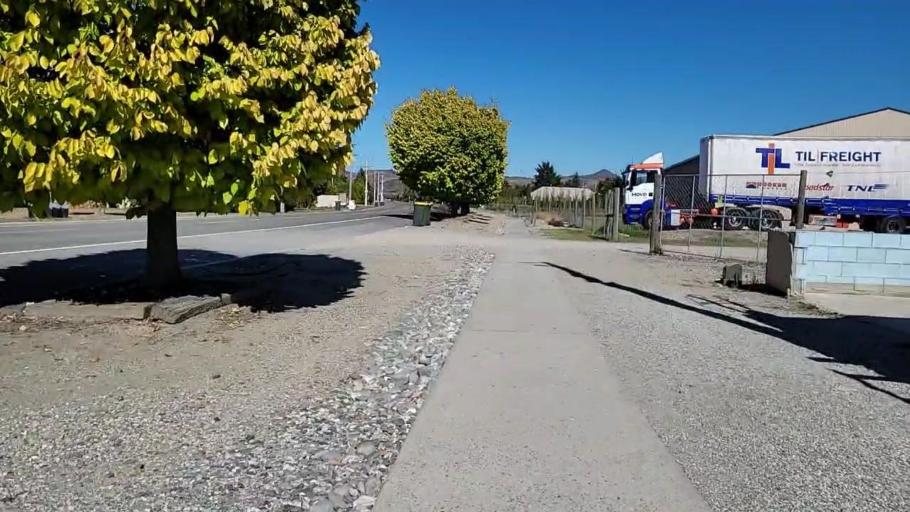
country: NZ
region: Otago
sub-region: Queenstown-Lakes District
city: Wanaka
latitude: -45.0977
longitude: 169.5983
